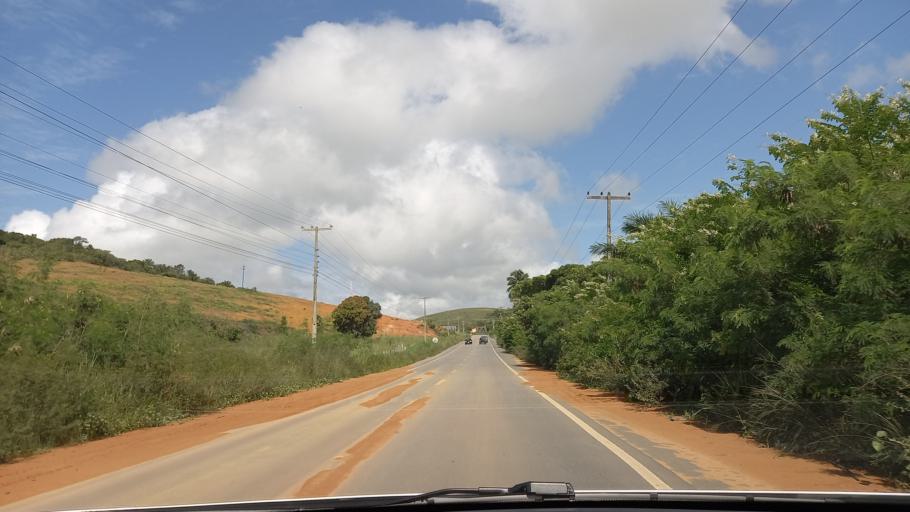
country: BR
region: Alagoas
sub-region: Maragogi
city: Maragogi
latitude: -8.9983
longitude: -35.2170
